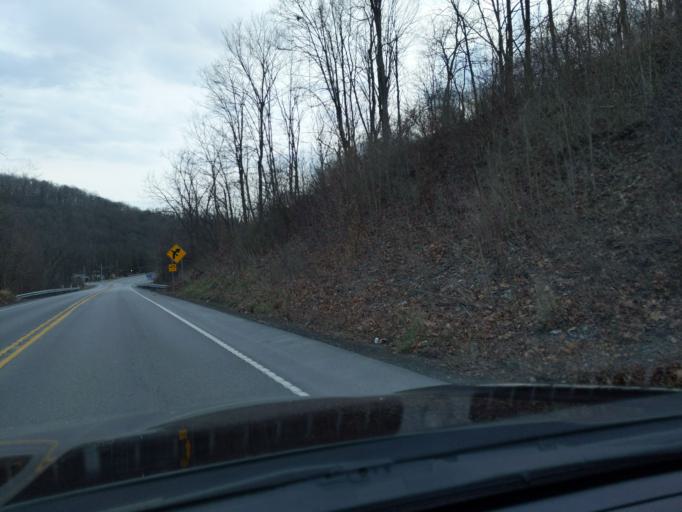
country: US
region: Pennsylvania
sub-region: Blair County
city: Lakemont
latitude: 40.4543
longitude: -78.3538
